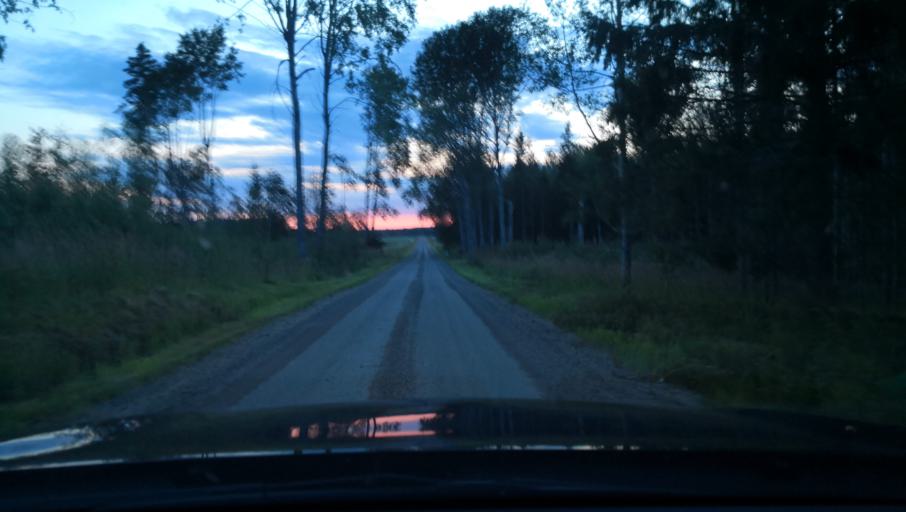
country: SE
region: Uppsala
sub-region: Osthammars Kommun
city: Bjorklinge
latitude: 60.0060
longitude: 17.3352
